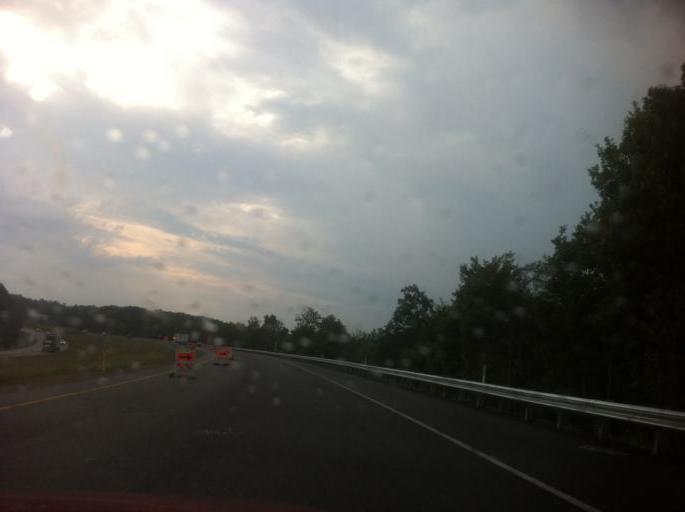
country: US
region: Pennsylvania
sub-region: Clarion County
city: Knox
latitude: 41.1998
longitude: -79.4854
